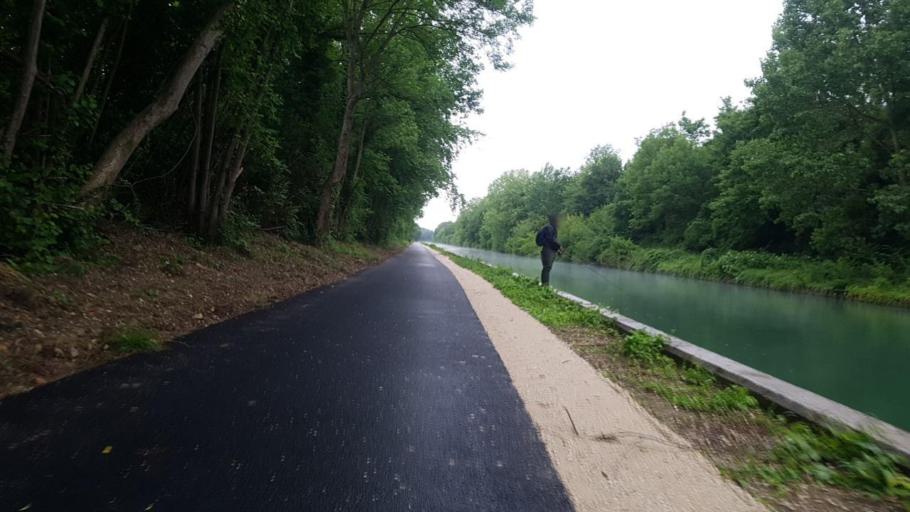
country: FR
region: Champagne-Ardenne
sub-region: Departement de la Marne
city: Sarry
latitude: 48.8640
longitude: 4.4722
